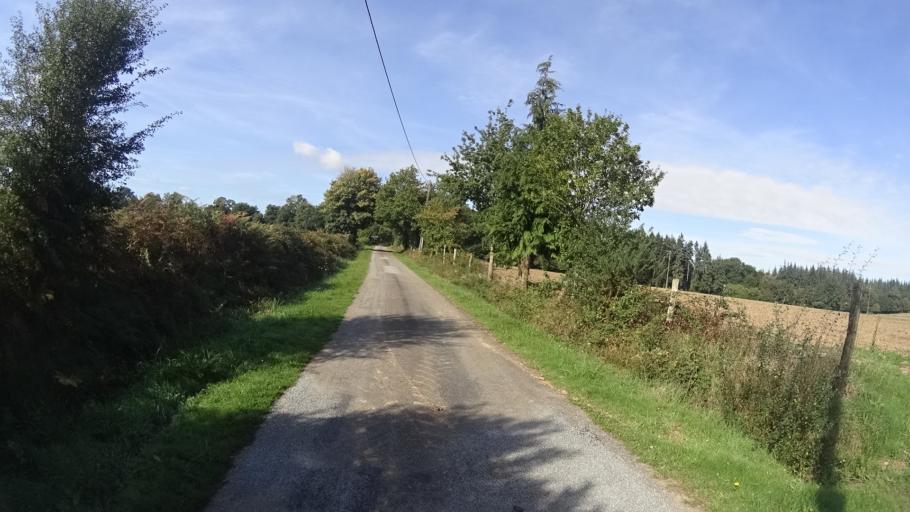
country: FR
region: Brittany
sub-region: Departement du Morbihan
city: Saint-Martin-sur-Oust
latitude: 47.7560
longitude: -2.2144
